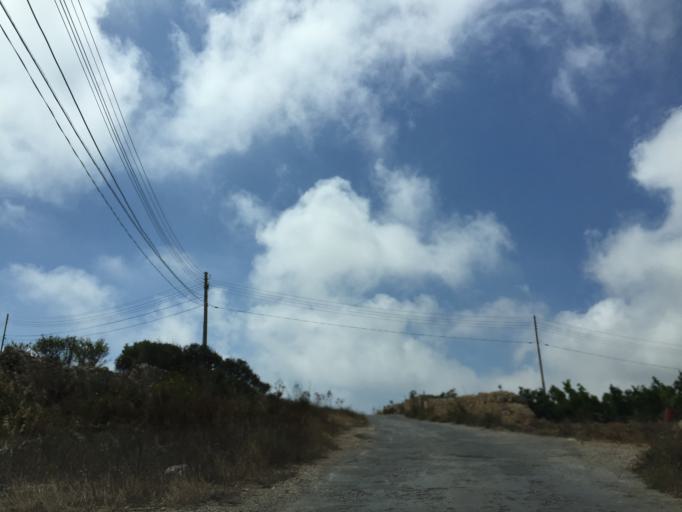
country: MT
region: Dingli
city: Dingli
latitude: 35.8605
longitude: 14.3736
